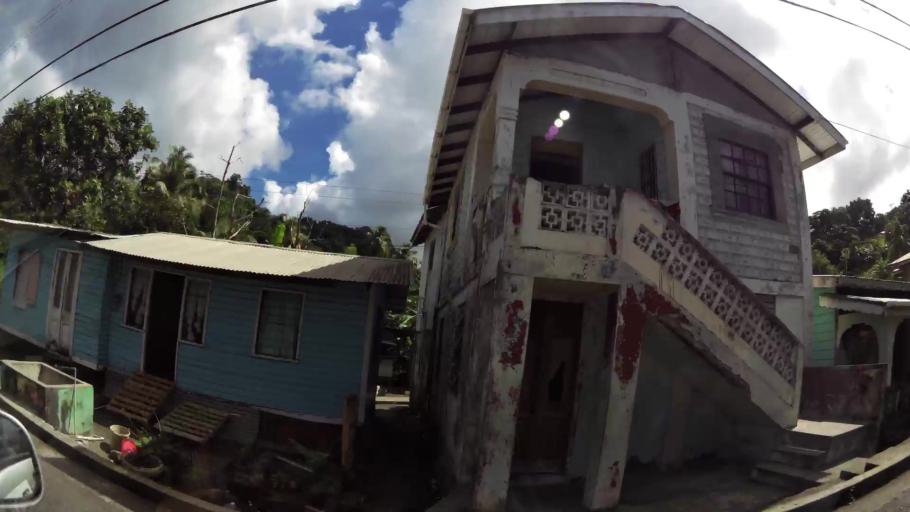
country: GD
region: Saint Mark
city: Victoria
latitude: 12.1999
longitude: -61.7019
